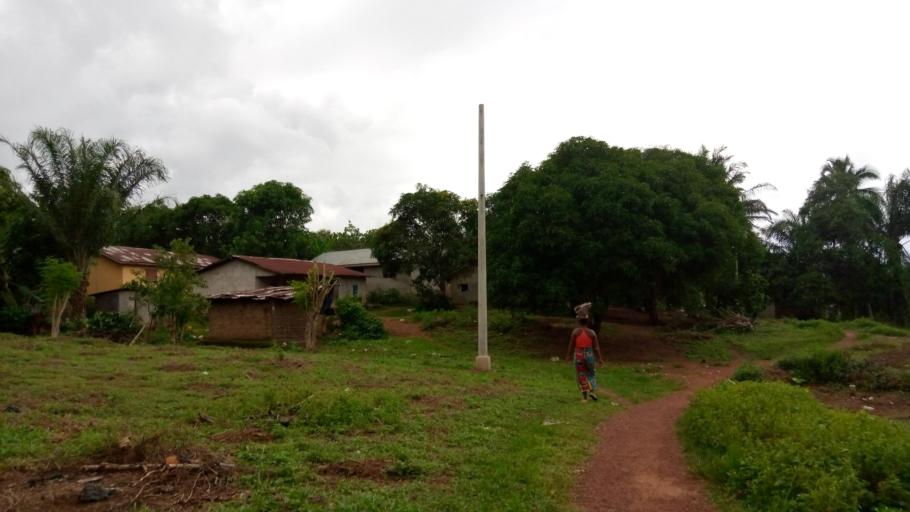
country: SL
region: Southern Province
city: Moyamba
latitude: 8.1654
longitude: -12.4406
